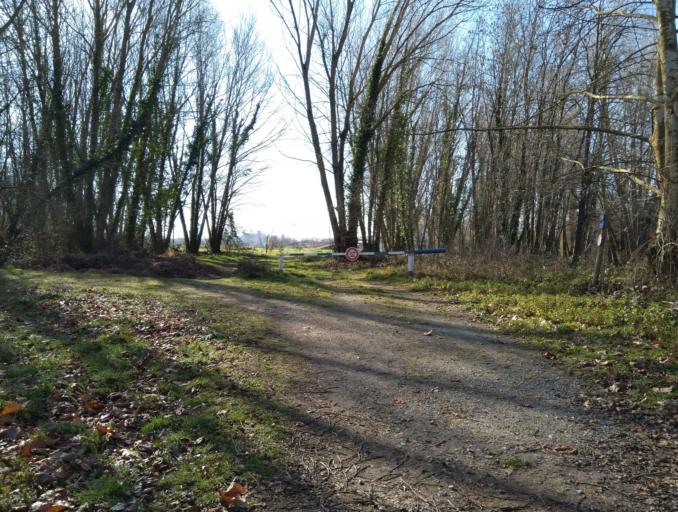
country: FR
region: Midi-Pyrenees
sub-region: Departement des Hautes-Pyrenees
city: Andrest
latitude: 43.3347
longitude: 0.0942
